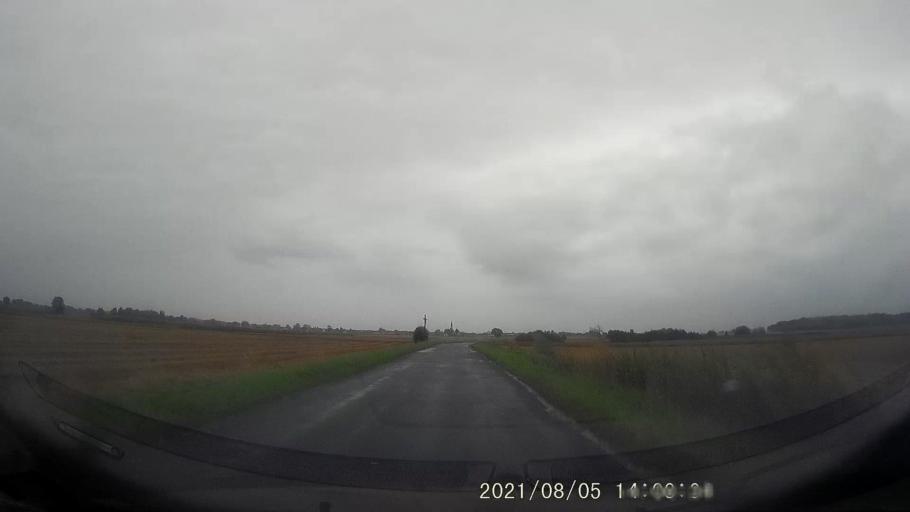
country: PL
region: Opole Voivodeship
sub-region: Powiat krapkowicki
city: Strzeleczki
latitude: 50.4695
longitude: 17.8143
